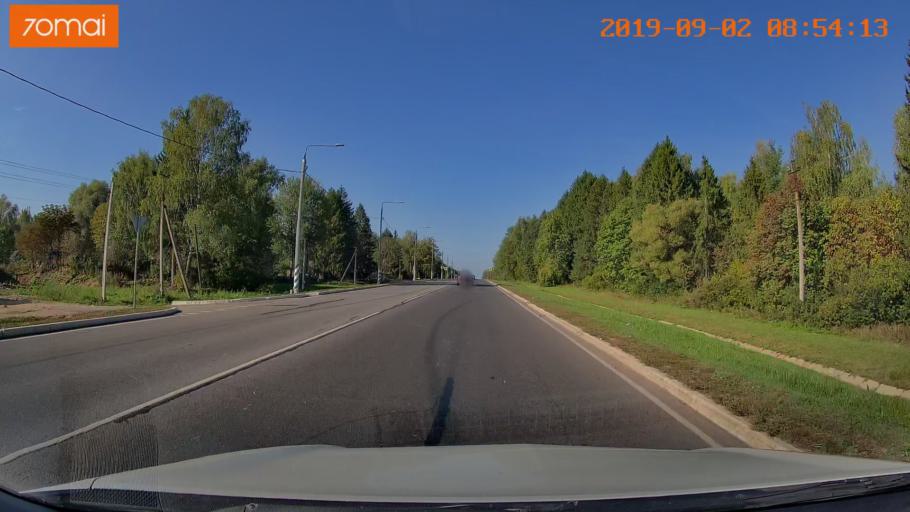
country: RU
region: Kaluga
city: Medyn'
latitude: 54.9630
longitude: 35.8433
